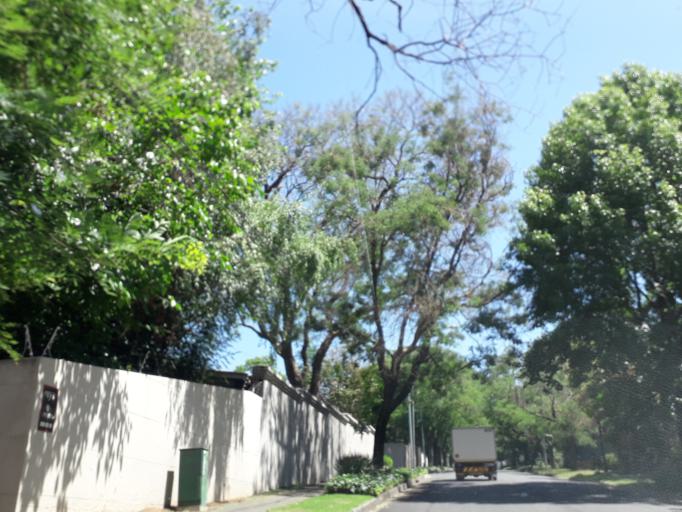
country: ZA
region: Gauteng
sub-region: City of Johannesburg Metropolitan Municipality
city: Johannesburg
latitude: -26.1316
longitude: 28.0294
